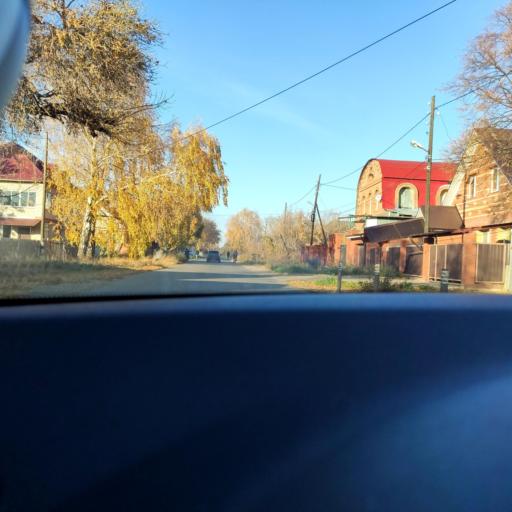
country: RU
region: Samara
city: Petra-Dubrava
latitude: 53.2549
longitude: 50.3291
